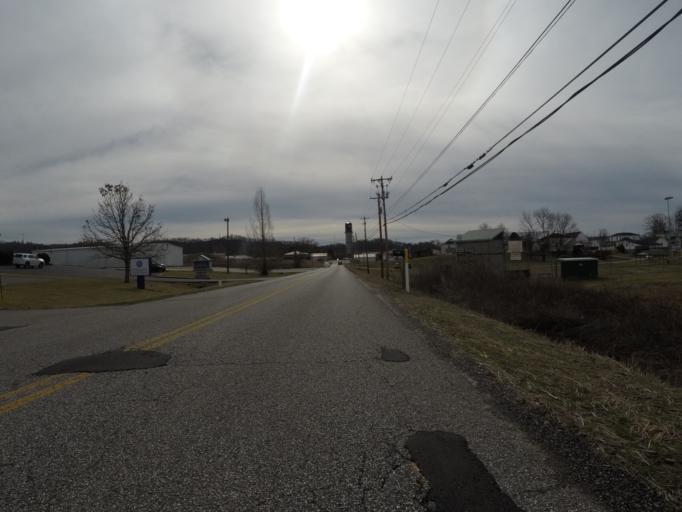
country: US
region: West Virginia
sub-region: Cabell County
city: Pea Ridge
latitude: 38.4406
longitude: -82.3767
